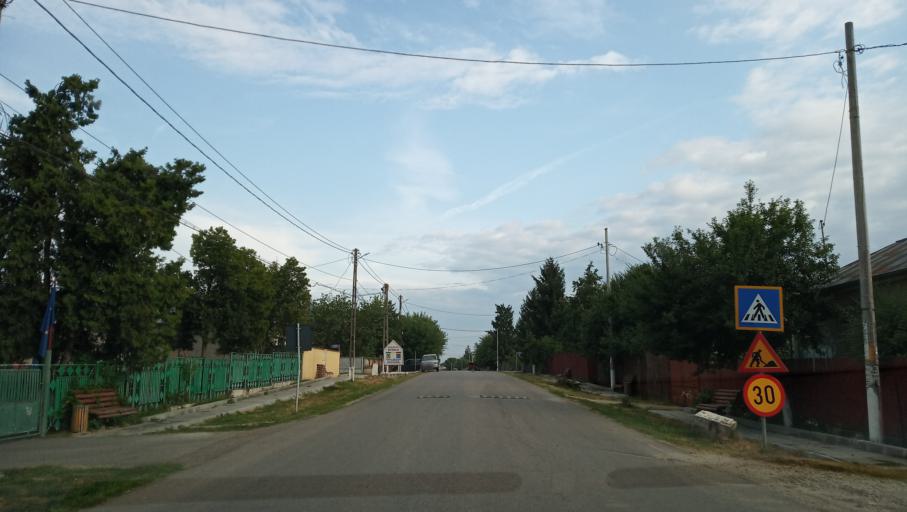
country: RO
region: Giurgiu
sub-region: Comuna Singureni
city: Singureni
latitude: 44.2334
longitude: 25.9436
